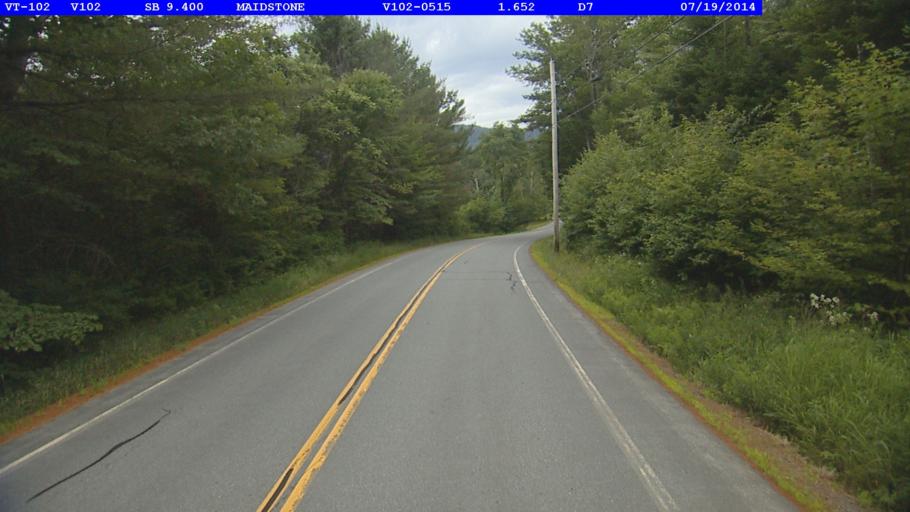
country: US
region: Vermont
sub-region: Essex County
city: Guildhall
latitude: 44.5917
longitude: -71.5509
